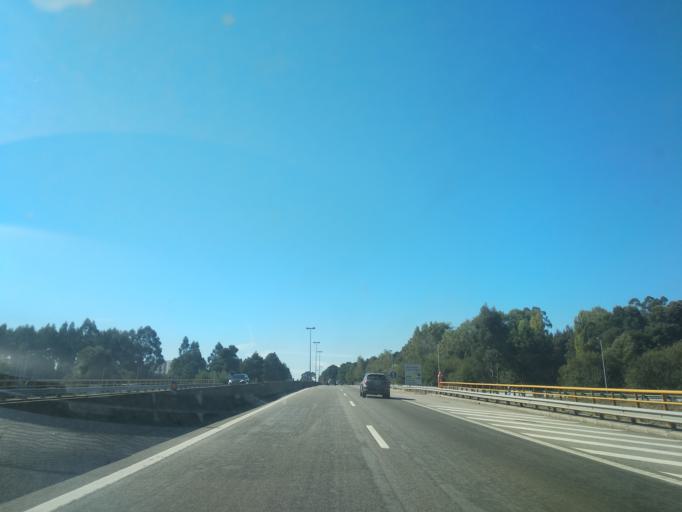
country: PT
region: Porto
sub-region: Vila Nova de Gaia
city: Perozinho
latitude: 41.0772
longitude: -8.5779
